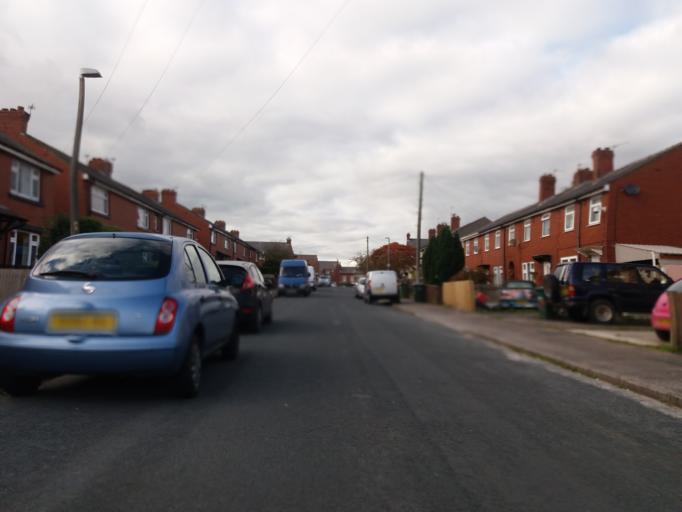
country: GB
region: England
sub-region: Lancashire
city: Chorley
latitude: 53.6462
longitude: -2.6283
